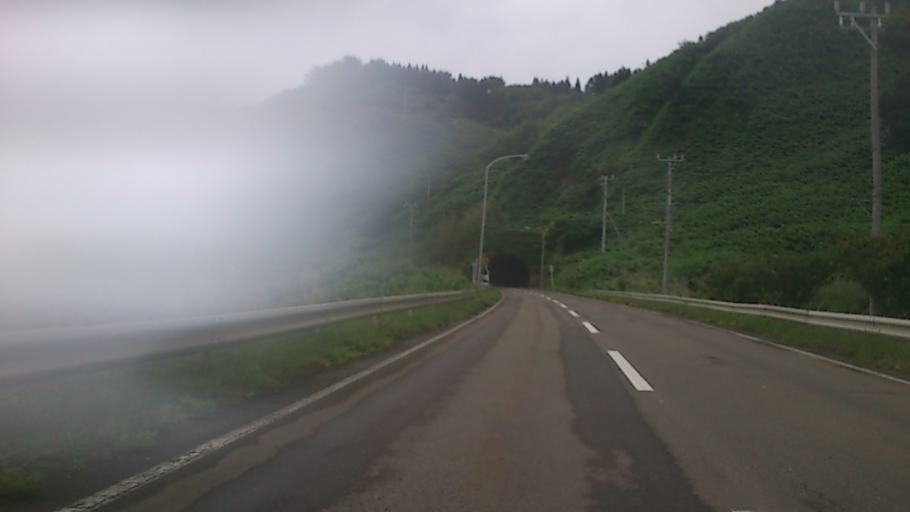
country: JP
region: Akita
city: Noshiromachi
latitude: 40.4779
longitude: 139.9484
